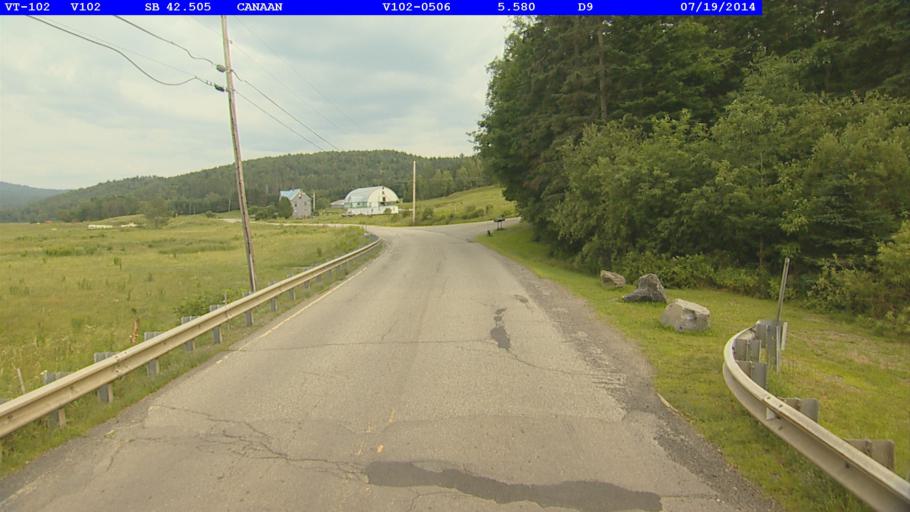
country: US
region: New Hampshire
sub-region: Coos County
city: Colebrook
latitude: 44.9793
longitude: -71.5419
